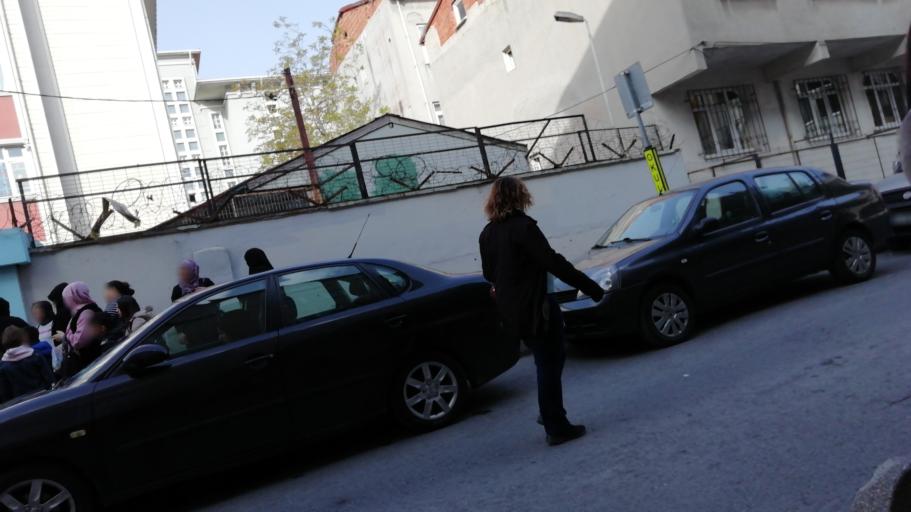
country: TR
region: Istanbul
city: Bagcilar
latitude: 41.0269
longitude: 28.8422
